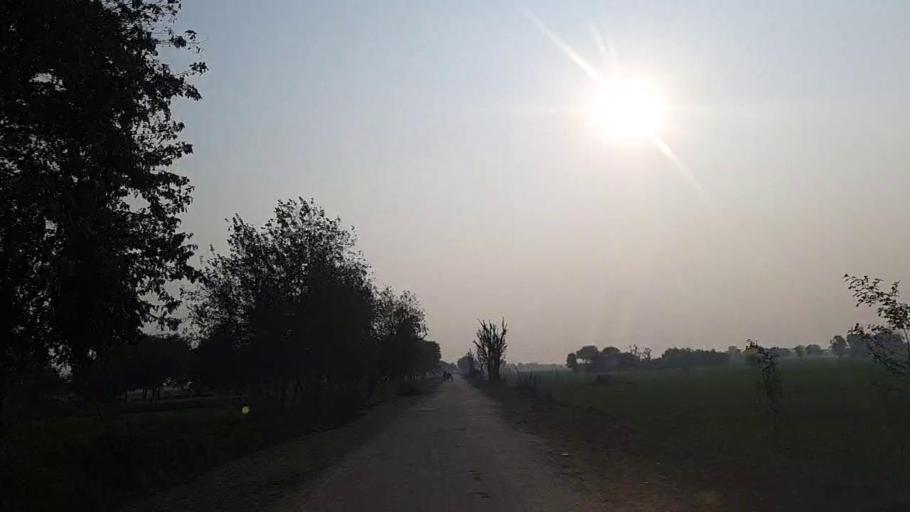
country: PK
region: Sindh
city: Nawabshah
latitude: 26.2285
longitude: 68.4829
